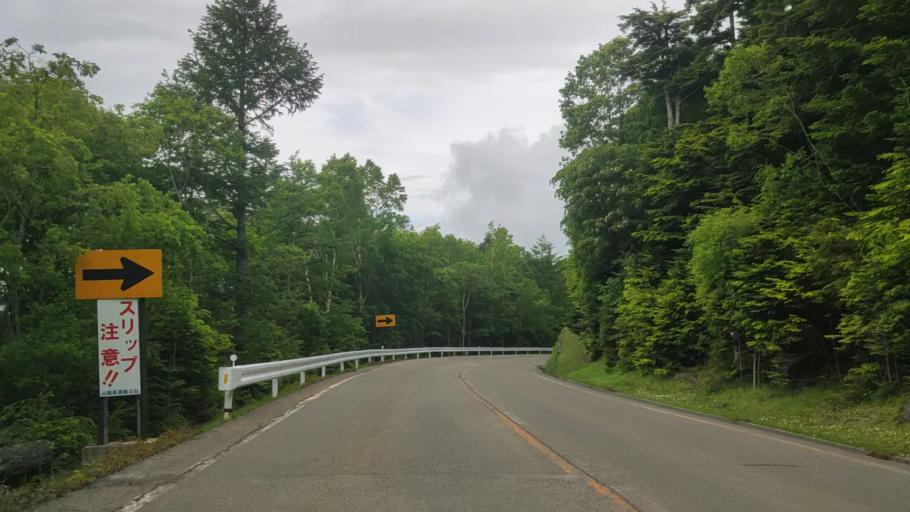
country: JP
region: Yamanashi
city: Fujikawaguchiko
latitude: 35.4045
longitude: 138.6984
